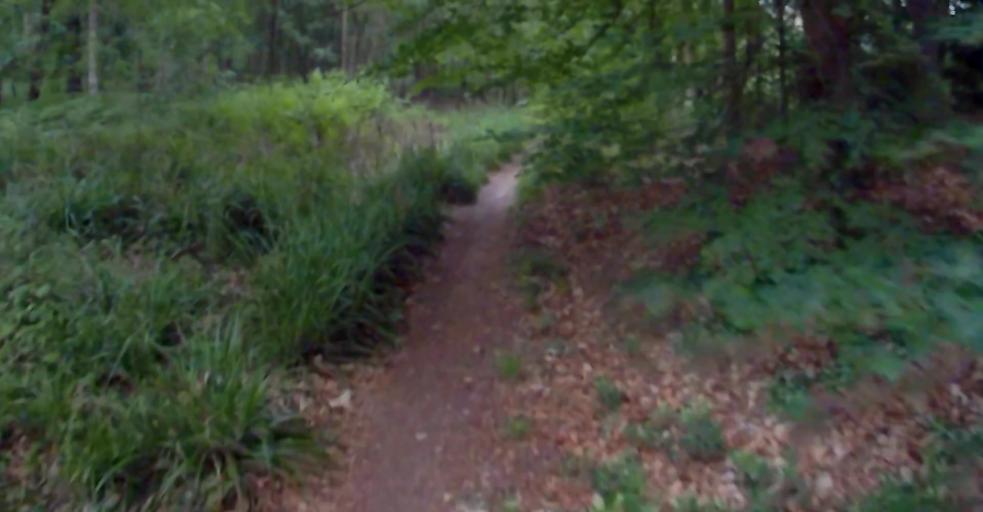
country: GB
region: England
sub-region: Hampshire
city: Fleet
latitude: 51.2748
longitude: -0.8055
